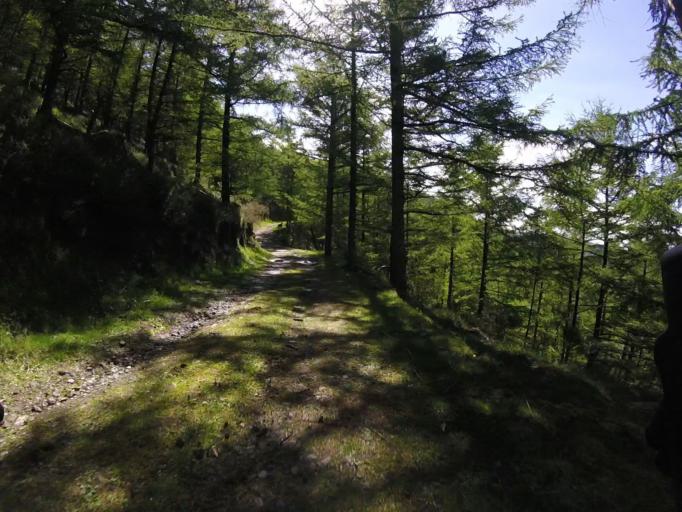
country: ES
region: Navarre
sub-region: Provincia de Navarra
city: Arano
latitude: 43.1839
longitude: -1.9527
